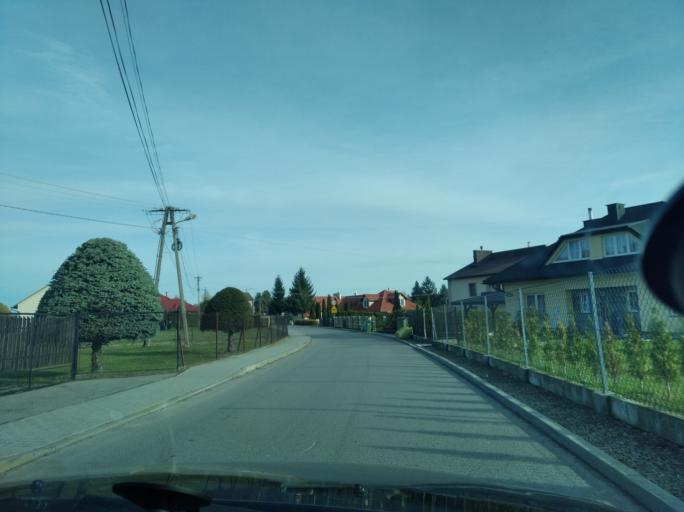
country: PL
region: Subcarpathian Voivodeship
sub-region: Powiat rzeszowski
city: Krasne
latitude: 50.0092
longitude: 22.0932
